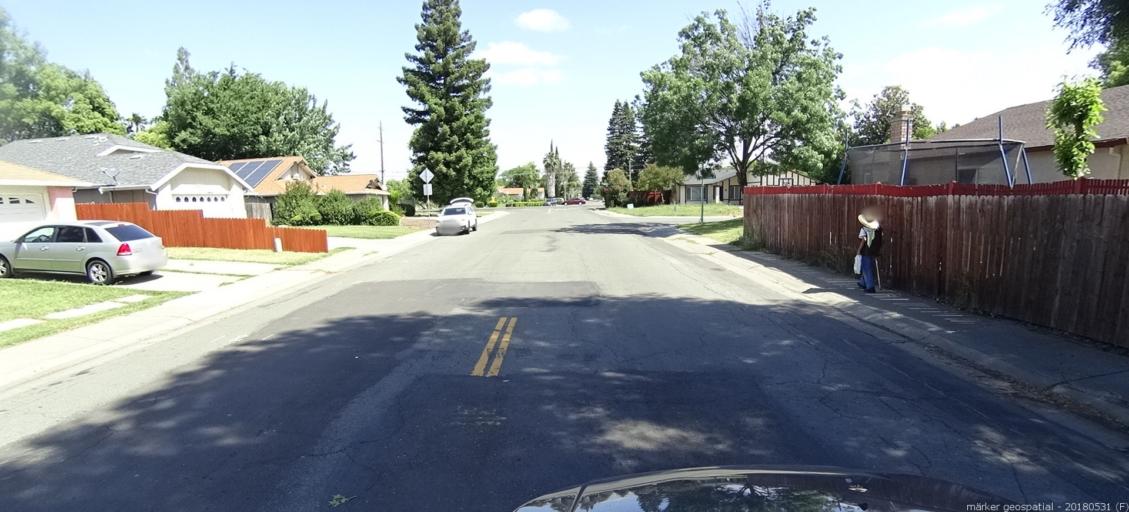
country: US
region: California
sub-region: Sacramento County
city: Sacramento
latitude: 38.6268
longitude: -121.4925
